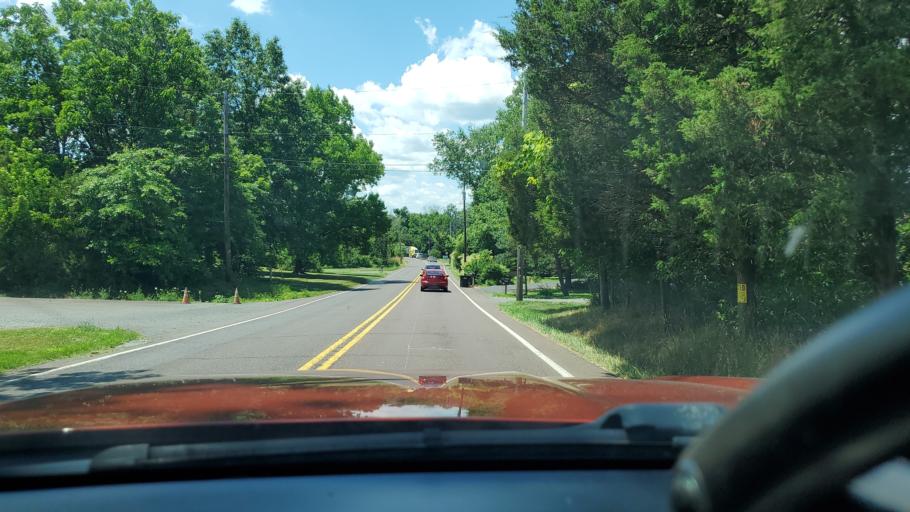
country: US
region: Pennsylvania
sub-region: Montgomery County
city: Gilbertsville
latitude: 40.3192
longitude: -75.5616
